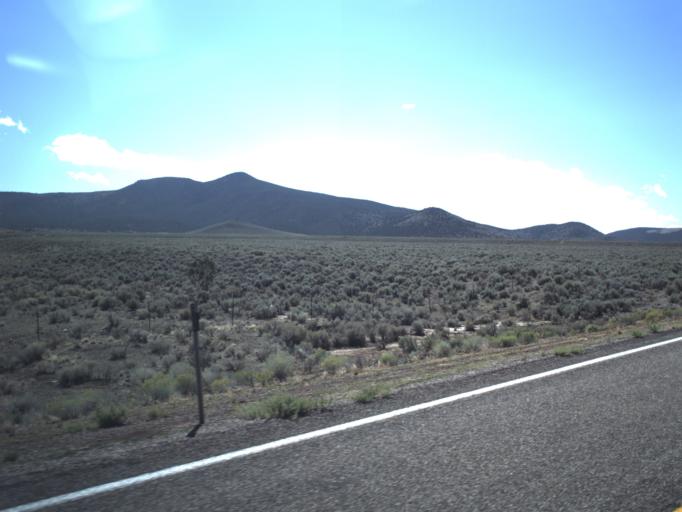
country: US
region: Utah
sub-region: Beaver County
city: Milford
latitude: 38.1872
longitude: -112.9396
